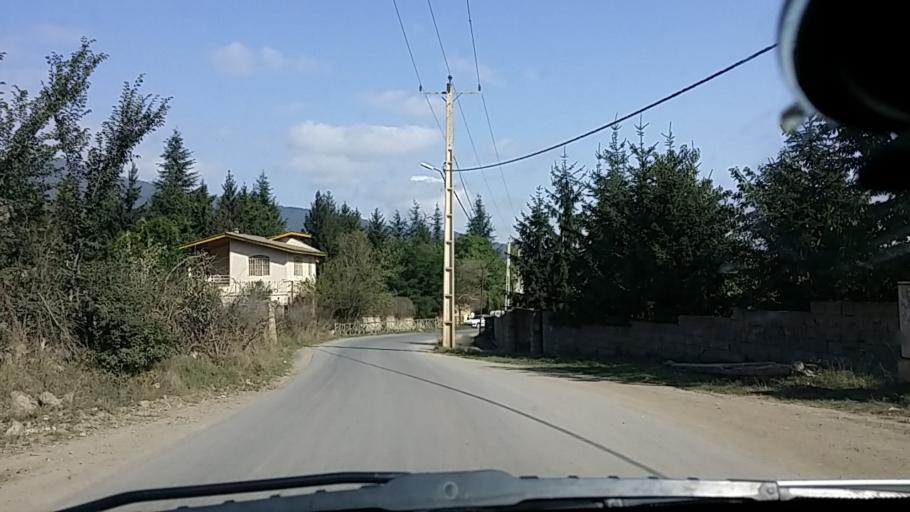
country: IR
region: Mazandaran
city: `Abbasabad
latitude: 36.5032
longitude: 51.1728
